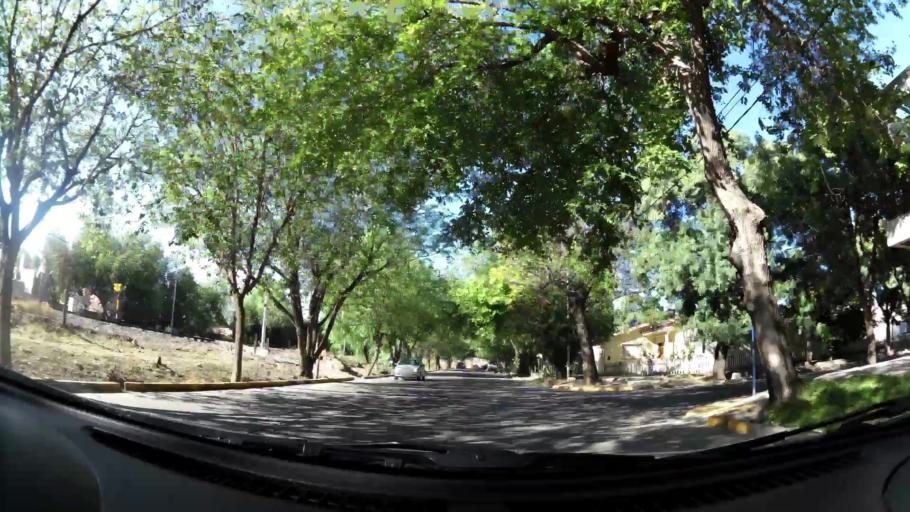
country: AR
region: Mendoza
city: Mendoza
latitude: -32.8724
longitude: -68.8457
